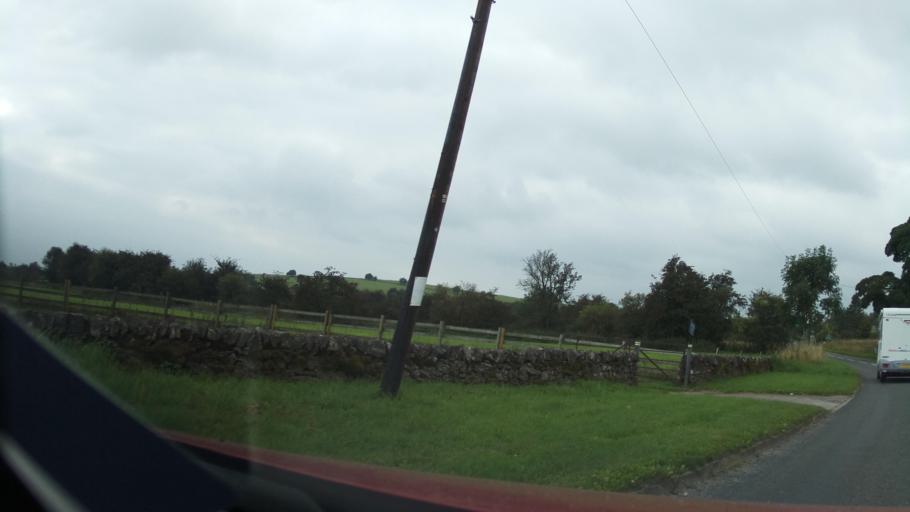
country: GB
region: England
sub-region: Staffordshire
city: Mayfield
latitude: 53.0283
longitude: -1.8764
